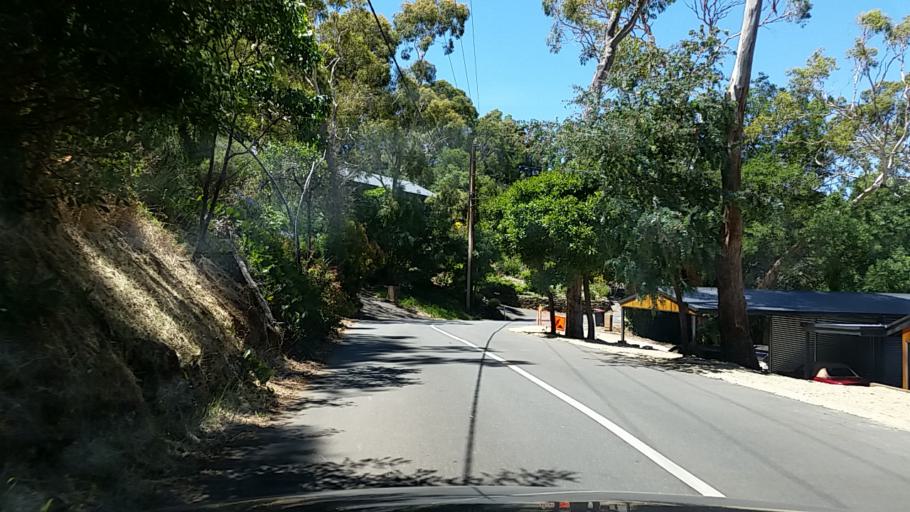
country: AU
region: South Australia
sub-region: Burnside
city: Mount Osmond
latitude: -34.9658
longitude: 138.6600
